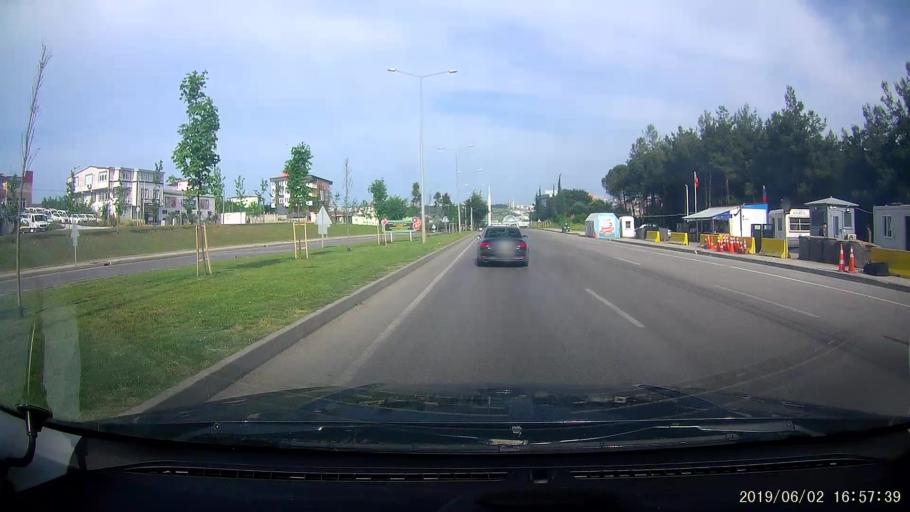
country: TR
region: Samsun
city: Samsun
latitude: 41.2905
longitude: 36.2762
